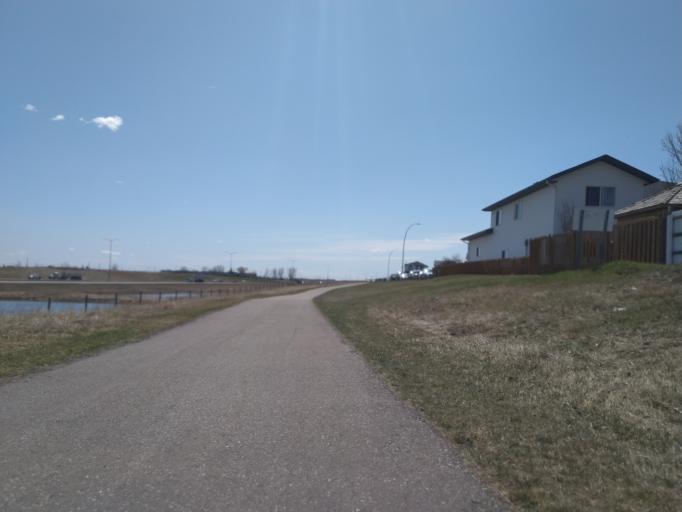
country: CA
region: Alberta
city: Chestermere
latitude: 51.0502
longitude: -113.9233
